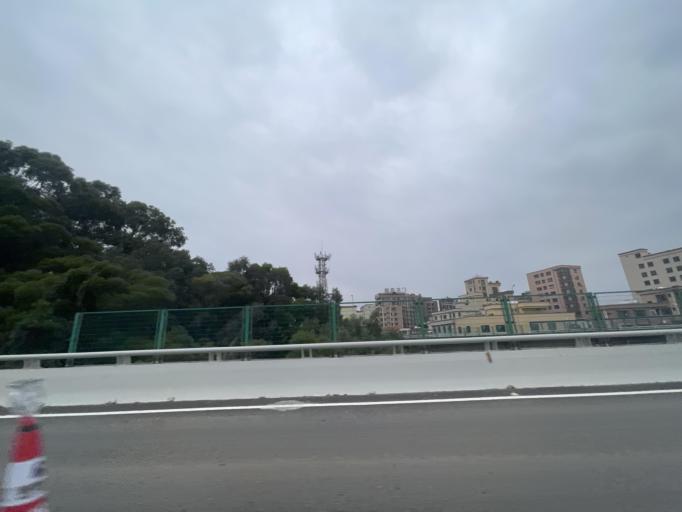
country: CN
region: Guangdong
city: Humen
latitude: 22.8070
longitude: 113.6605
